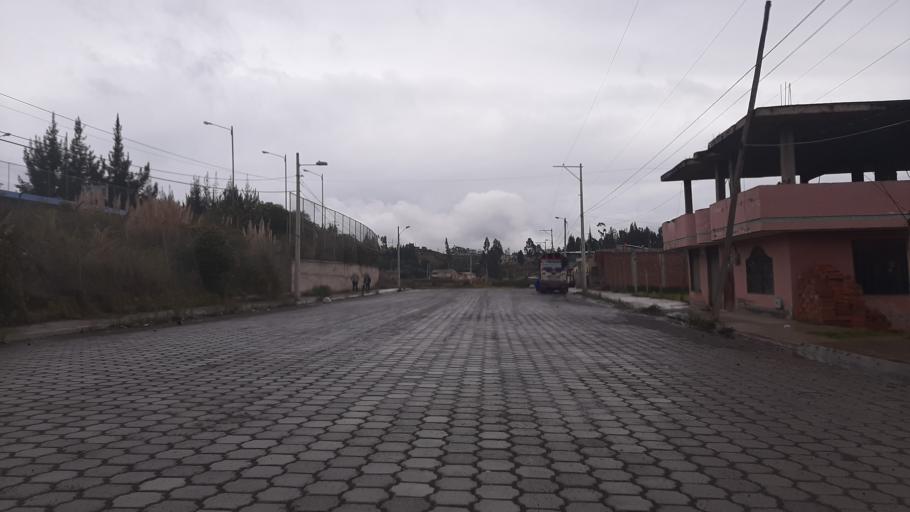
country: EC
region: Chimborazo
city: Riobamba
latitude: -1.6533
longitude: -78.6409
